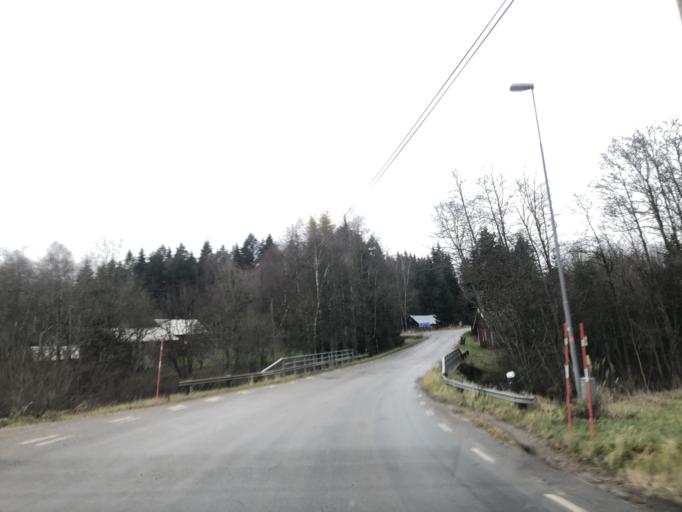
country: SE
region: Vaestra Goetaland
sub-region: Ulricehamns Kommun
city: Ulricehamn
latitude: 57.8770
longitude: 13.5324
